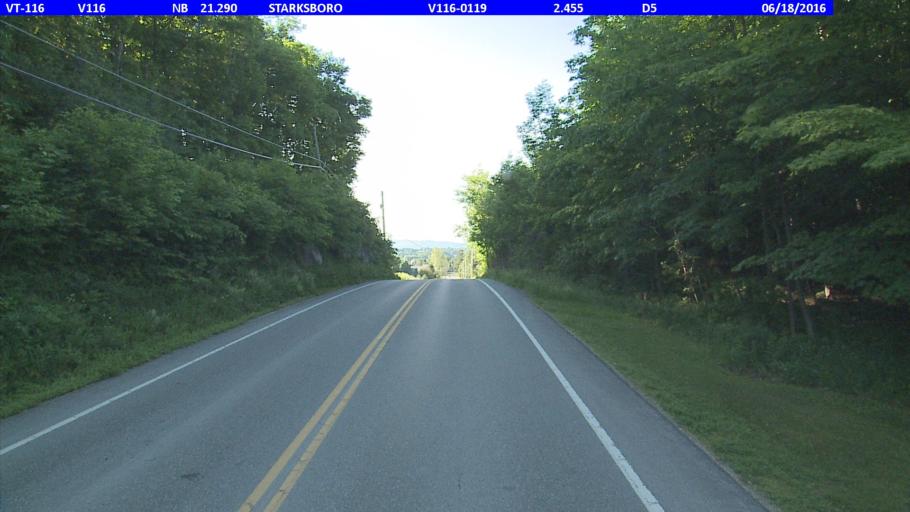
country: US
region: Vermont
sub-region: Addison County
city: Bristol
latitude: 44.2200
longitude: -73.0559
